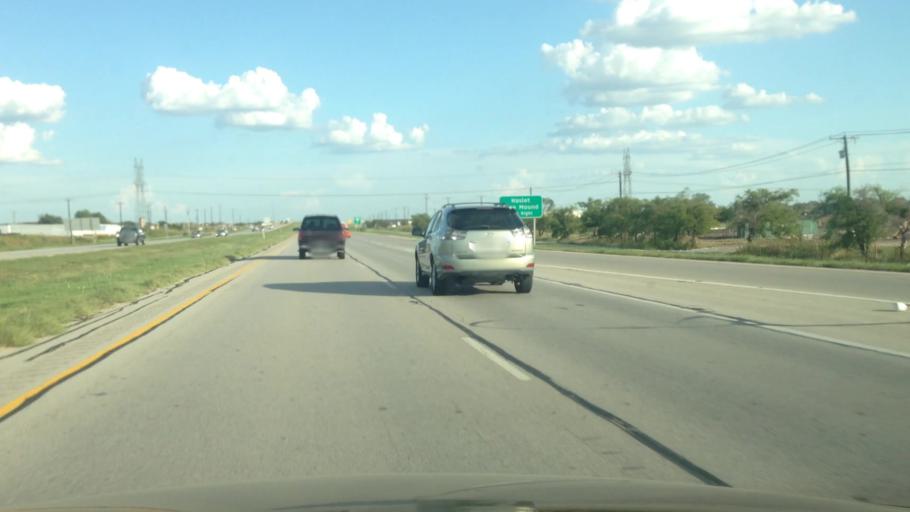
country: US
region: Texas
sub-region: Tarrant County
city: Haslet
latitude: 32.9220
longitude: -97.3553
